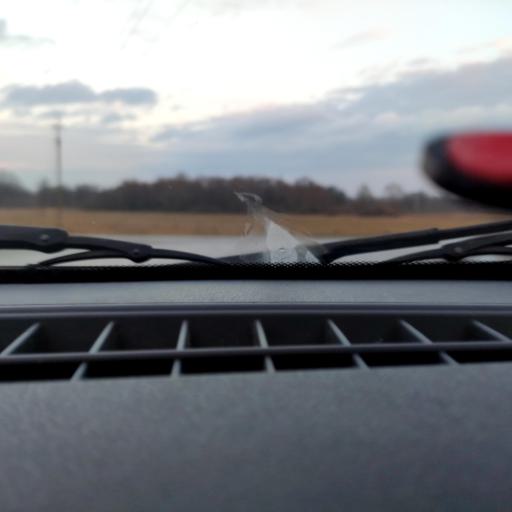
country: RU
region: Bashkortostan
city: Avdon
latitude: 54.5098
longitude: 55.8761
